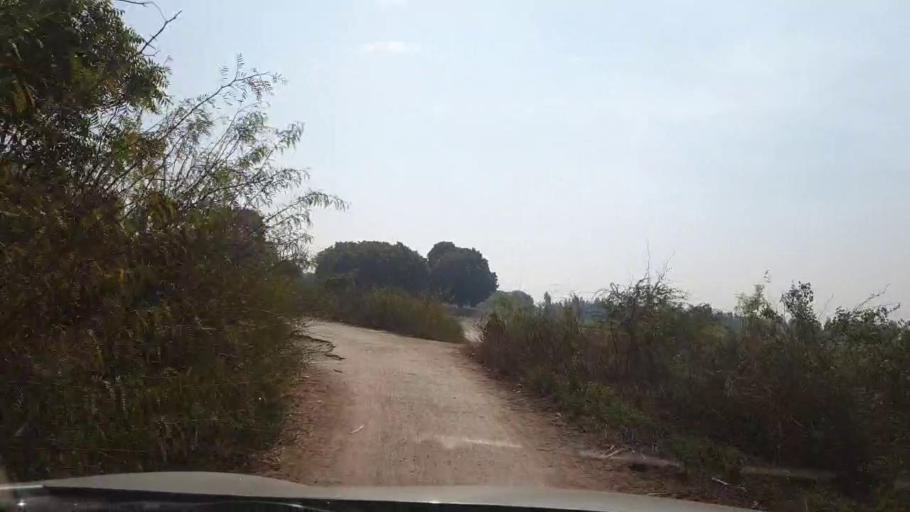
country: PK
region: Sindh
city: Tando Allahyar
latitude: 25.4689
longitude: 68.6426
